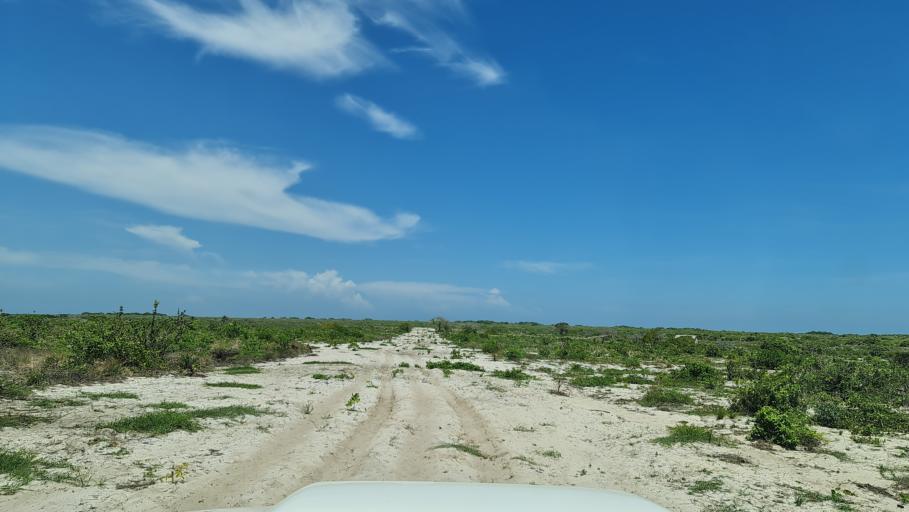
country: MZ
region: Nampula
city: Ilha de Mocambique
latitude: -15.1948
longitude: 40.6197
